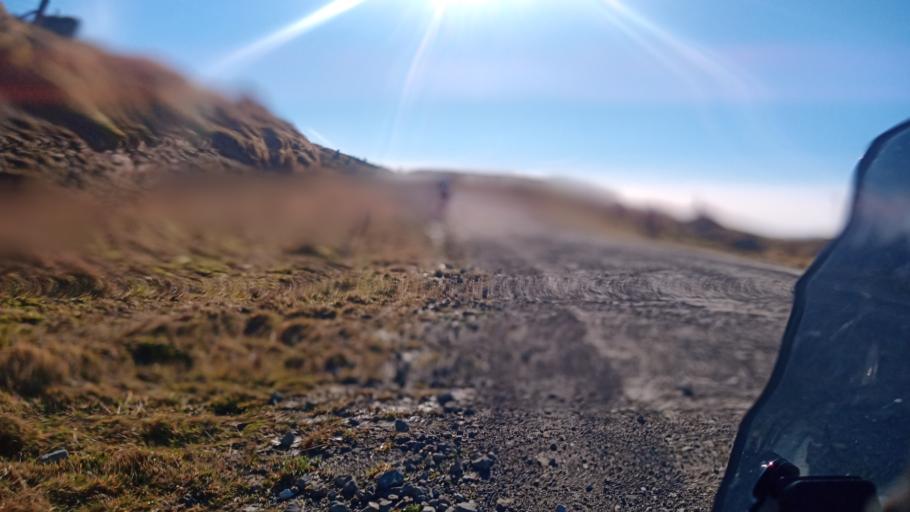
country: NZ
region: Gisborne
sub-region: Gisborne District
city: Gisborne
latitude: -38.1794
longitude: 177.8254
